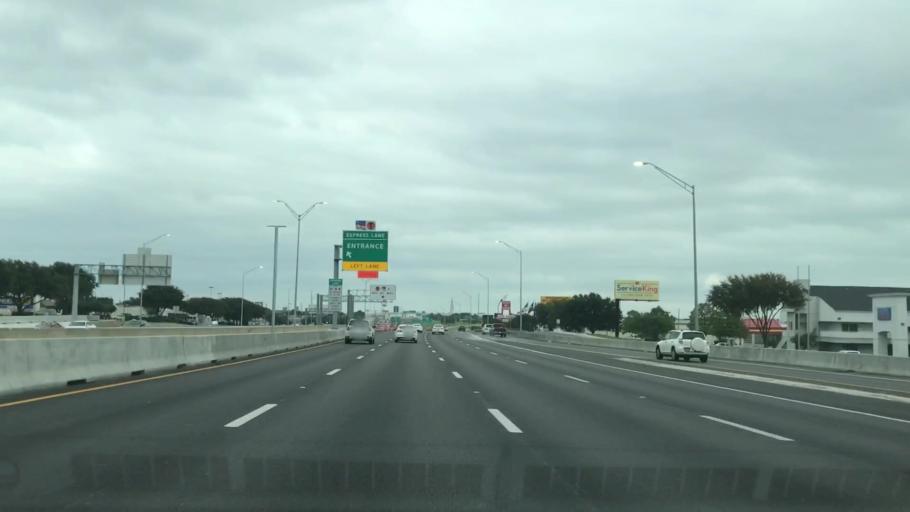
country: US
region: Texas
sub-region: Dallas County
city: Irving
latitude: 32.8371
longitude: -97.0046
